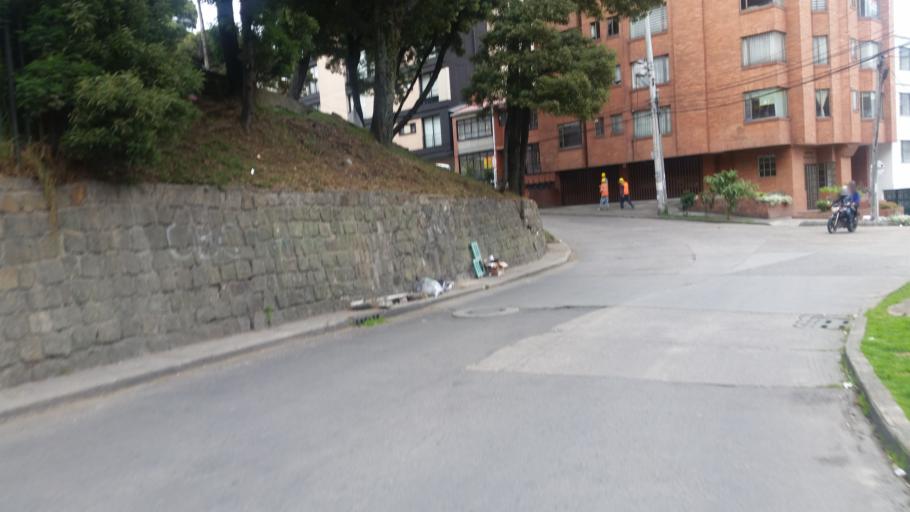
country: CO
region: Bogota D.C.
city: Bogota
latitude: 4.6376
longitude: -74.0622
